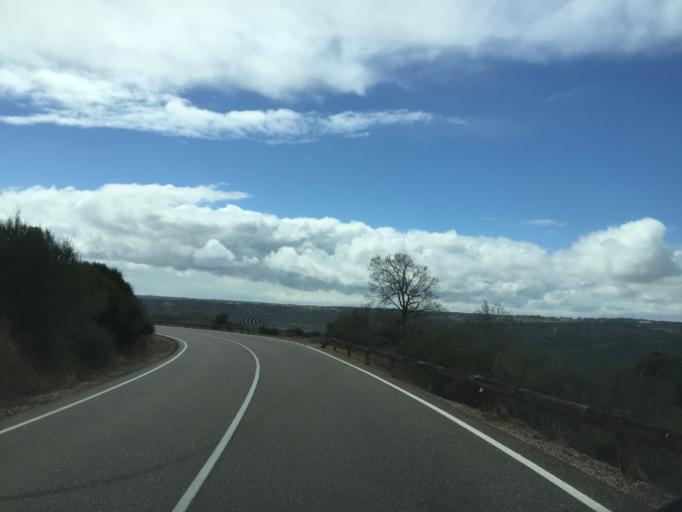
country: ES
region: Castille and Leon
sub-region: Provincia de Zamora
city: Villalcampo
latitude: 41.5046
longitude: -6.0789
